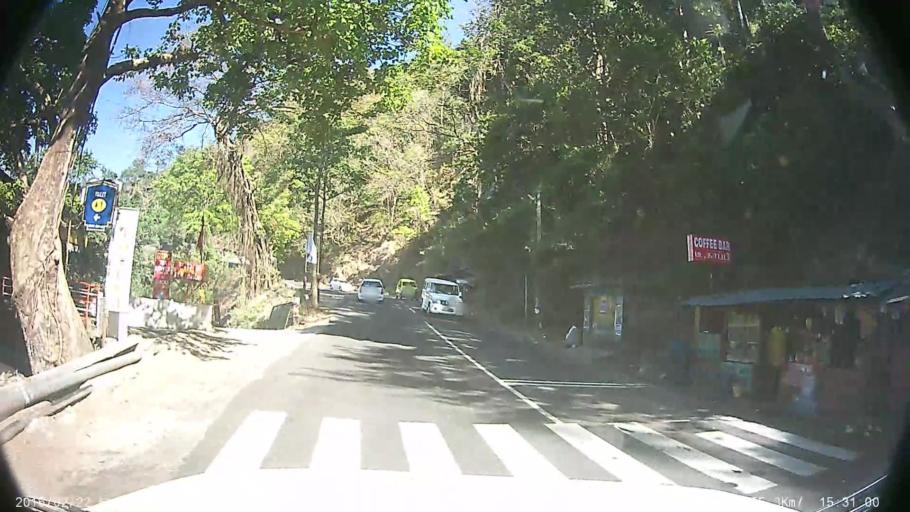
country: IN
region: Kerala
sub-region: Kottayam
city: Erattupetta
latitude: 9.5581
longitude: 76.9559
